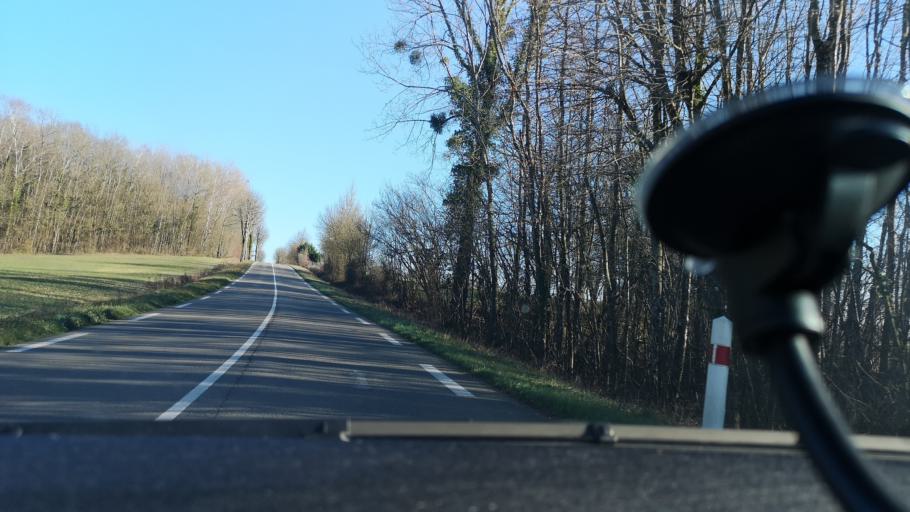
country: FR
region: Franche-Comte
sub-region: Departement du Jura
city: Bletterans
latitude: 46.7441
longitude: 5.4213
